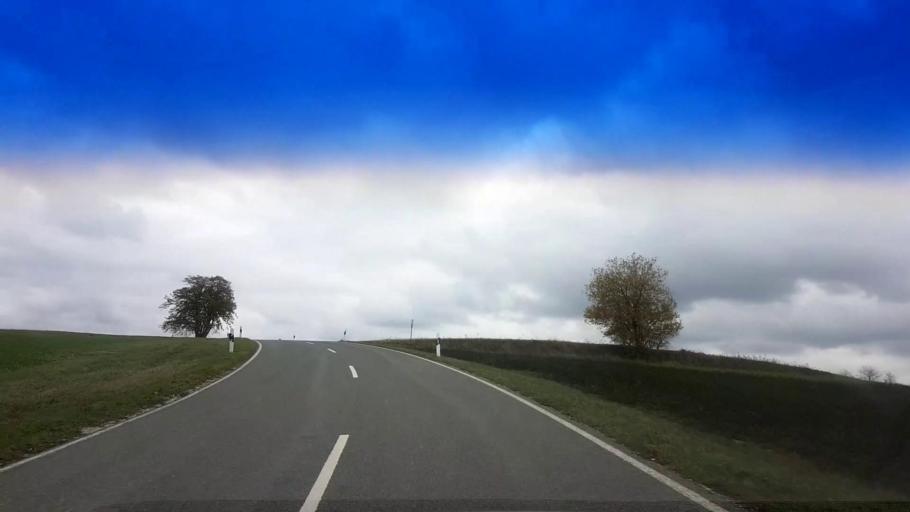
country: DE
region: Bavaria
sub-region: Upper Franconia
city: Poxdorf
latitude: 49.9417
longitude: 11.1090
